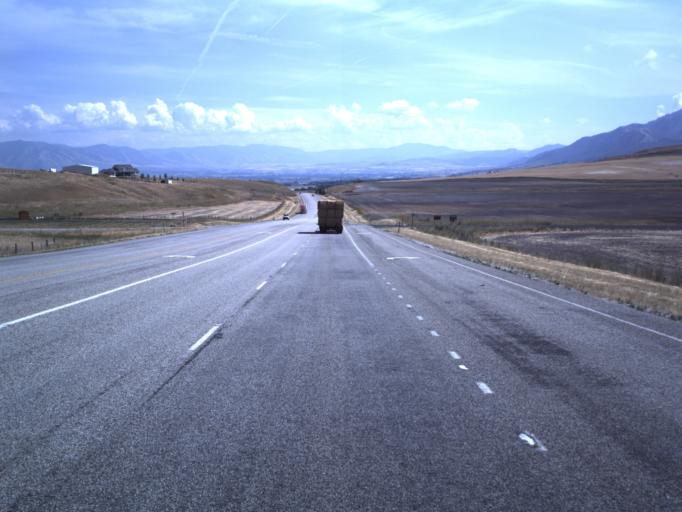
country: US
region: Utah
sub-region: Cache County
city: Mendon
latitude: 41.7770
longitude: -112.0207
